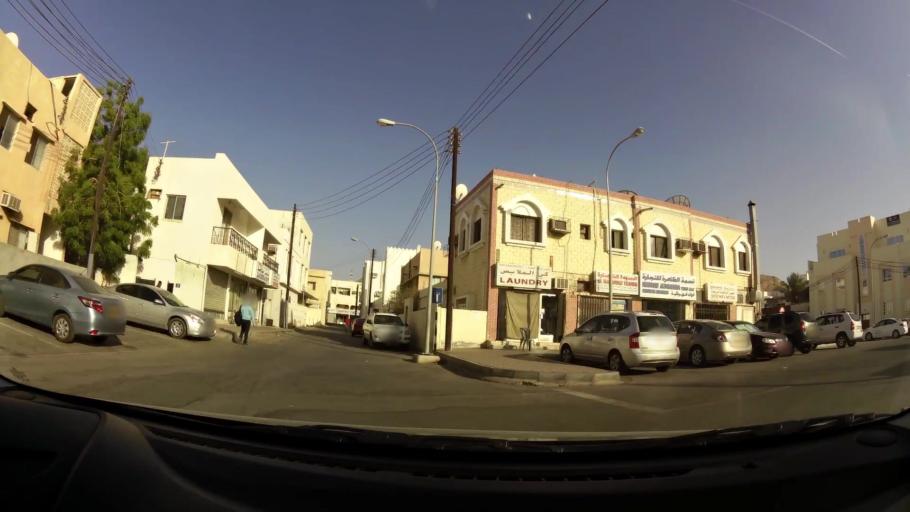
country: OM
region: Muhafazat Masqat
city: Muscat
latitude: 23.5888
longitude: 58.5510
